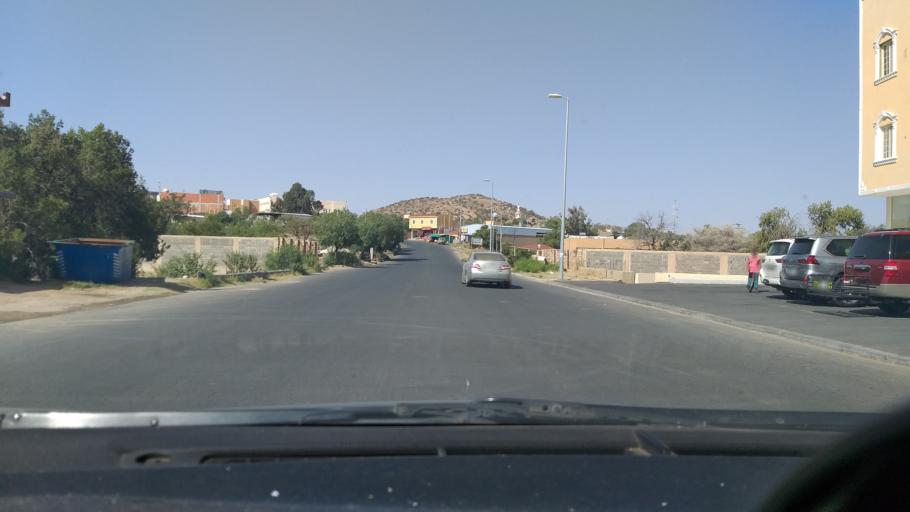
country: SA
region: Makkah
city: Ash Shafa
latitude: 21.0676
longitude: 40.3229
